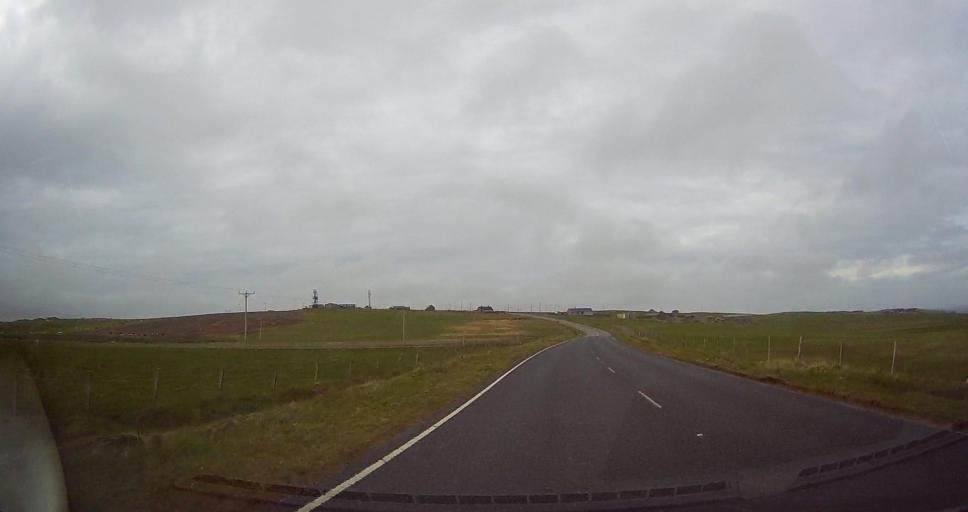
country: GB
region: Scotland
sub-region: Shetland Islands
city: Sandwick
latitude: 59.9065
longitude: -1.3022
